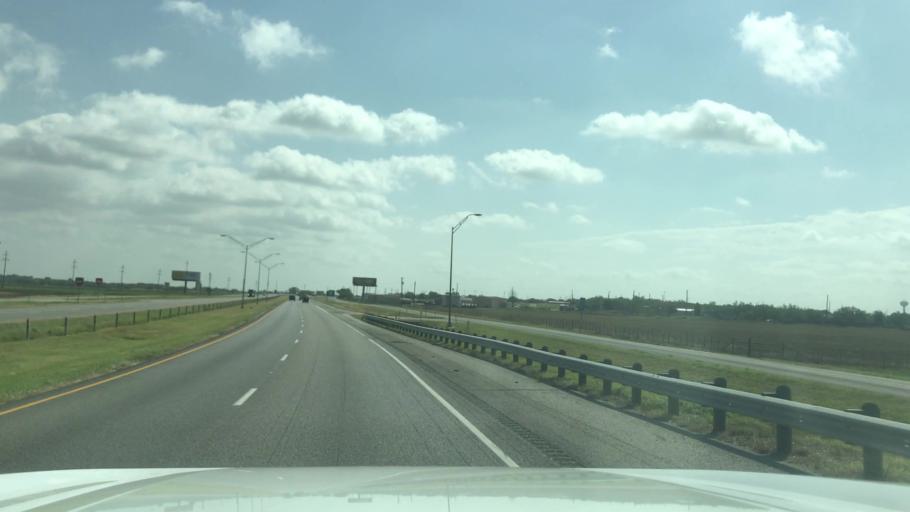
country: US
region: Texas
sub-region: Taylor County
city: Merkel
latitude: 32.4751
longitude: -100.0285
